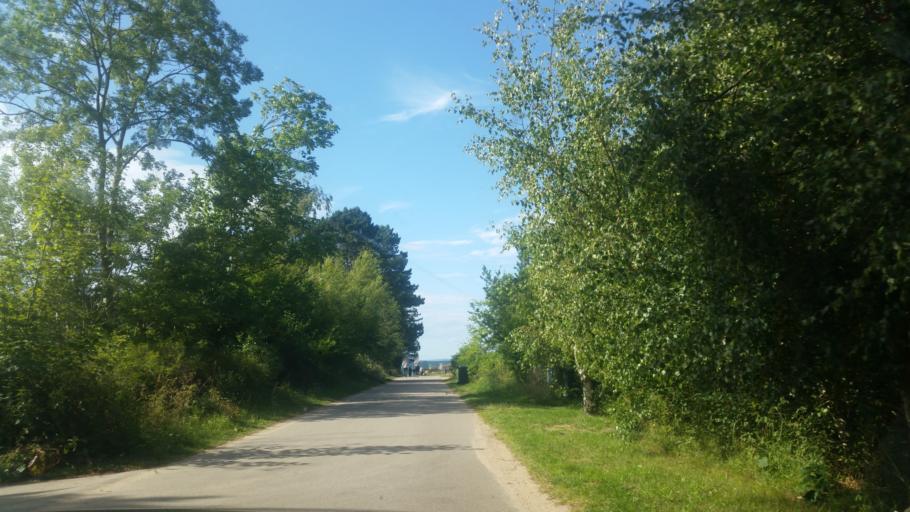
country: DK
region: Zealand
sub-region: Odsherred Kommune
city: Horve
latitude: 55.8289
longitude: 11.3960
